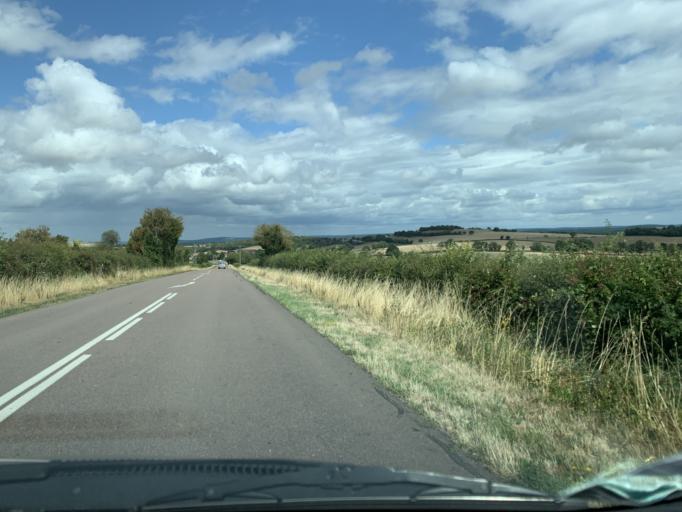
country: FR
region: Bourgogne
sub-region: Departement de la Nievre
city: Varzy
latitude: 47.3819
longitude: 3.4370
